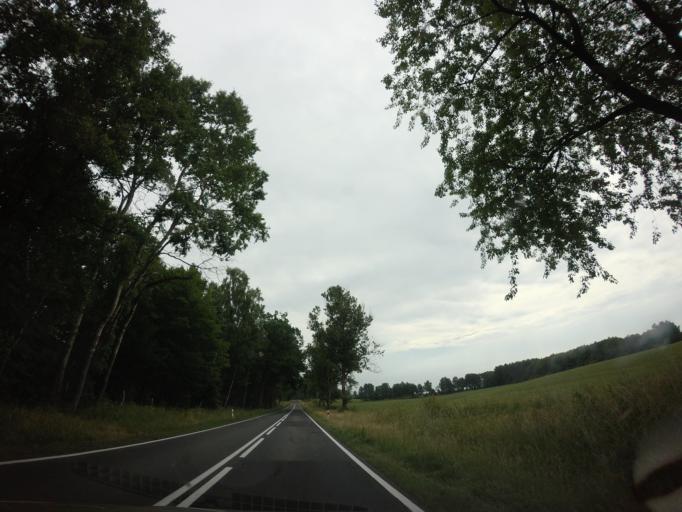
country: PL
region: West Pomeranian Voivodeship
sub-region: Powiat szczecinecki
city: Lubowo
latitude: 53.5909
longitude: 16.3416
